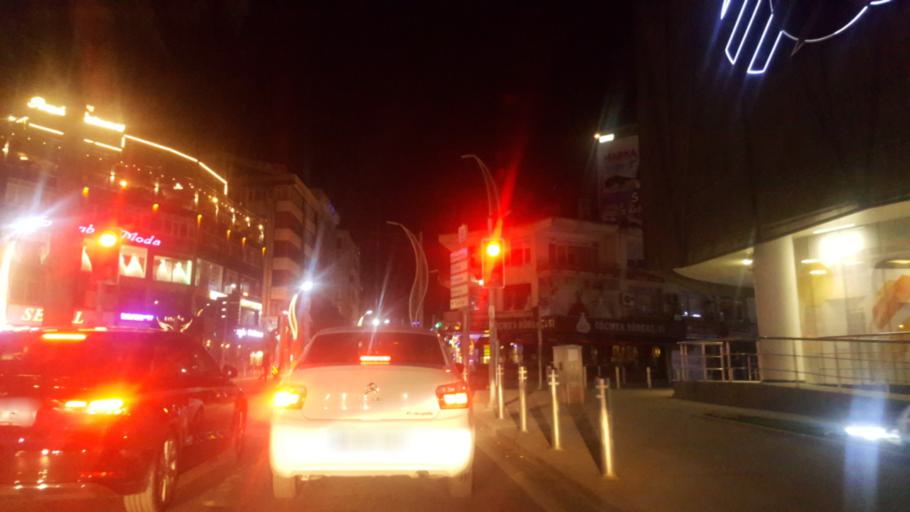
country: TR
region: Kocaeli
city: Gebze
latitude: 40.7960
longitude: 29.4324
